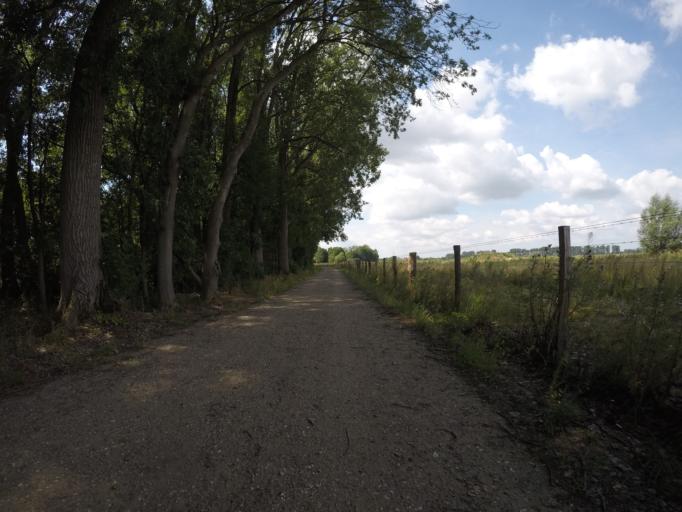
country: DE
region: North Rhine-Westphalia
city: Rees
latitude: 51.7673
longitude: 6.4451
